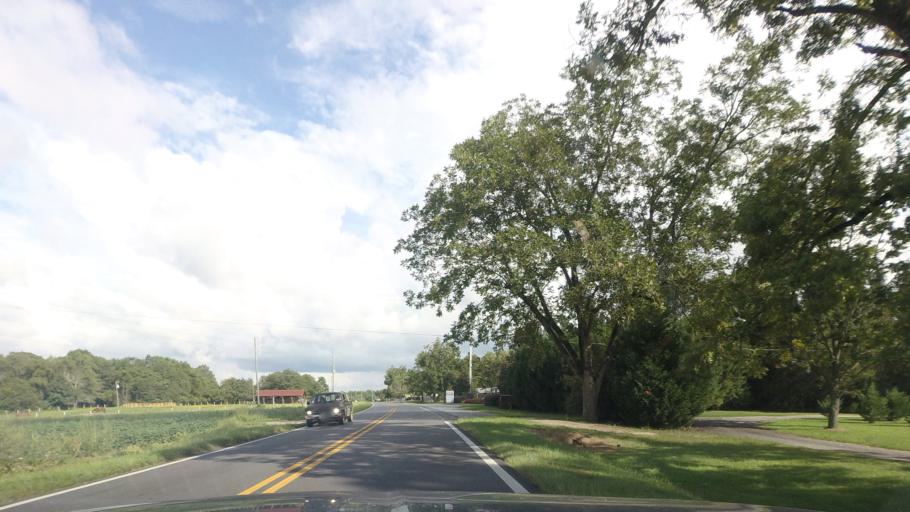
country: US
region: Georgia
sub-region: Peach County
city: Byron
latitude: 32.6377
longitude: -83.7360
